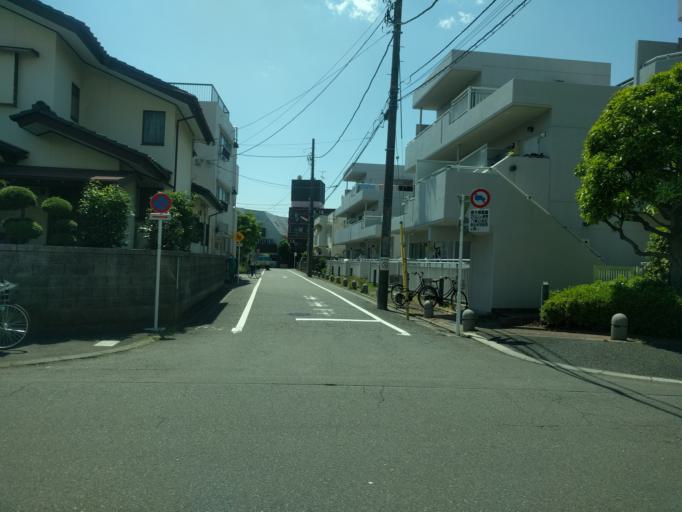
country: JP
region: Tokyo
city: Mitaka-shi
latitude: 35.6607
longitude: 139.6242
